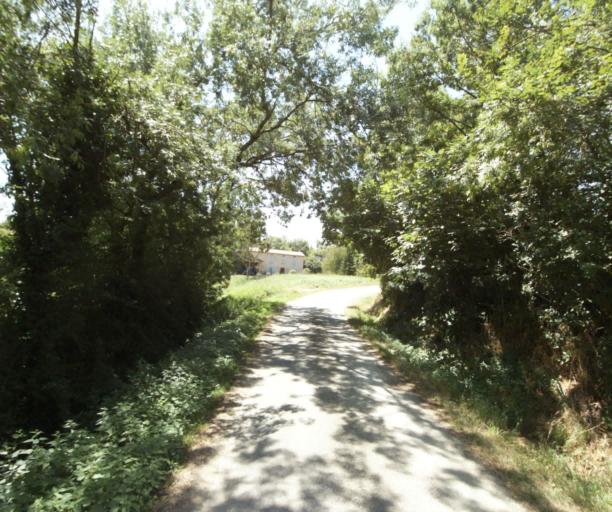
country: FR
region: Midi-Pyrenees
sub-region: Departement de la Haute-Garonne
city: Revel
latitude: 43.4991
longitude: 2.0310
